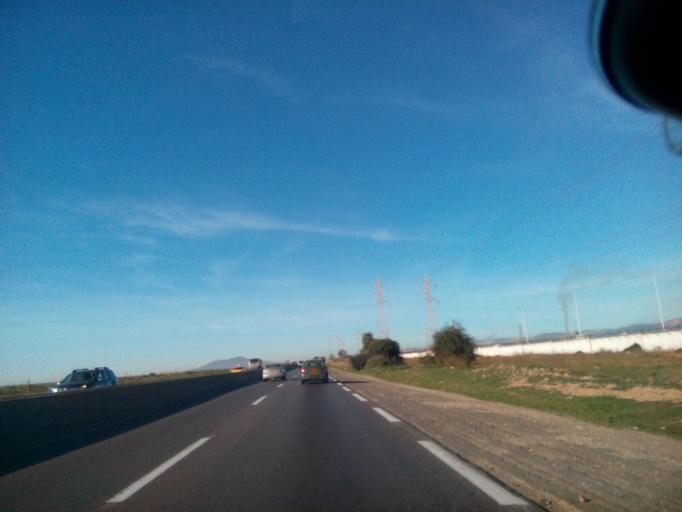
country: DZ
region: Oran
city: Ain el Bya
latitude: 35.8006
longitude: -0.3206
